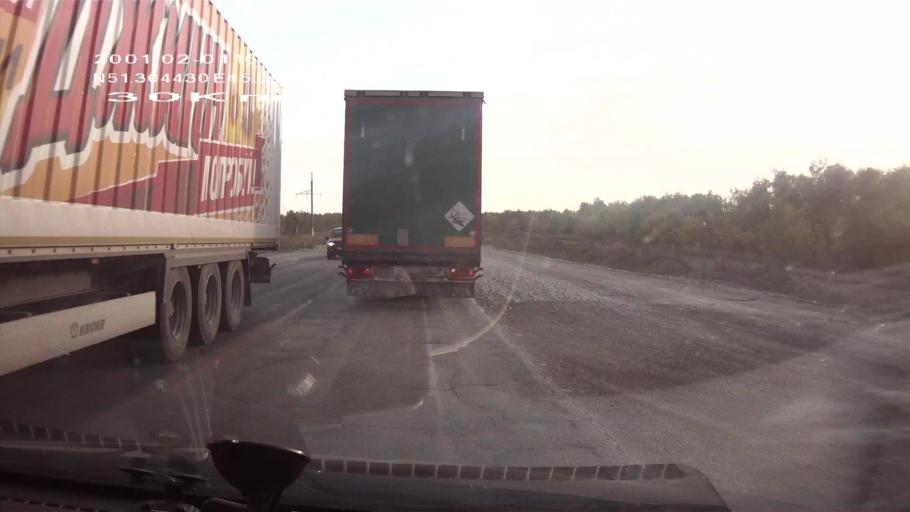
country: RU
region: Saratov
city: Krasnyy Oktyabr'
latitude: 51.3040
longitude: 45.6921
